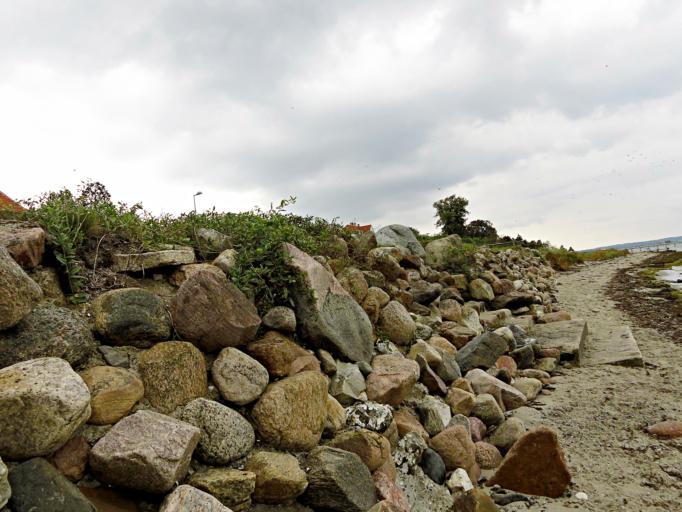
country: DK
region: Capital Region
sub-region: Horsholm Kommune
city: Horsholm
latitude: 55.8909
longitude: 12.5398
